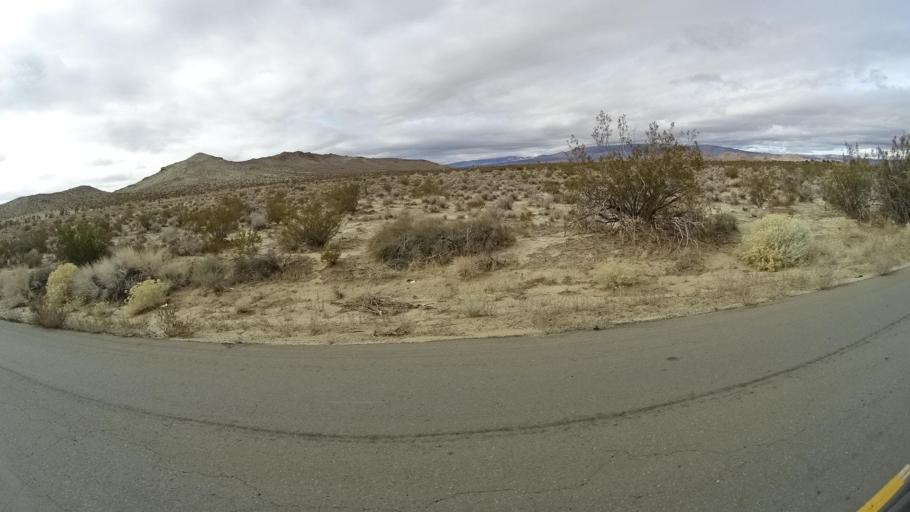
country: US
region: California
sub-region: Kern County
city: Rosamond
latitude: 34.9296
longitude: -118.2124
